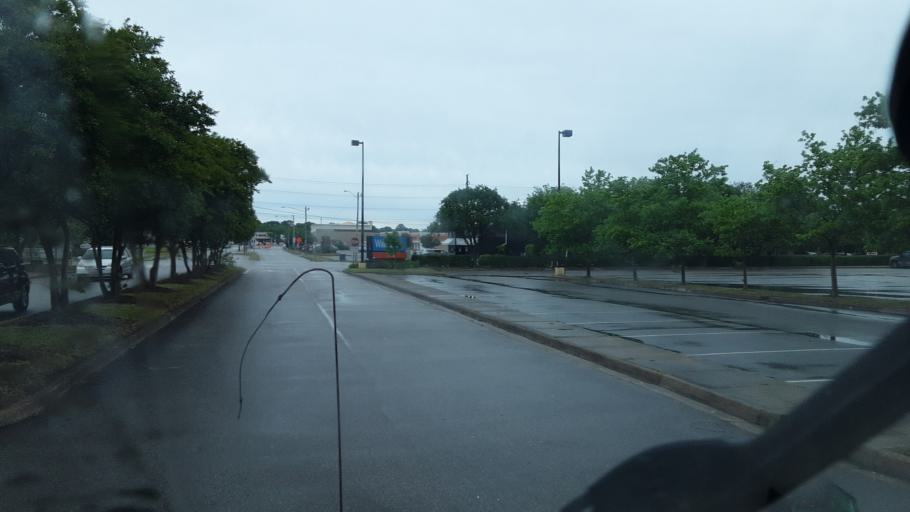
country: US
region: Virginia
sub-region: City of Virginia Beach
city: Virginia Beach
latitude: 36.8481
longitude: -76.0197
